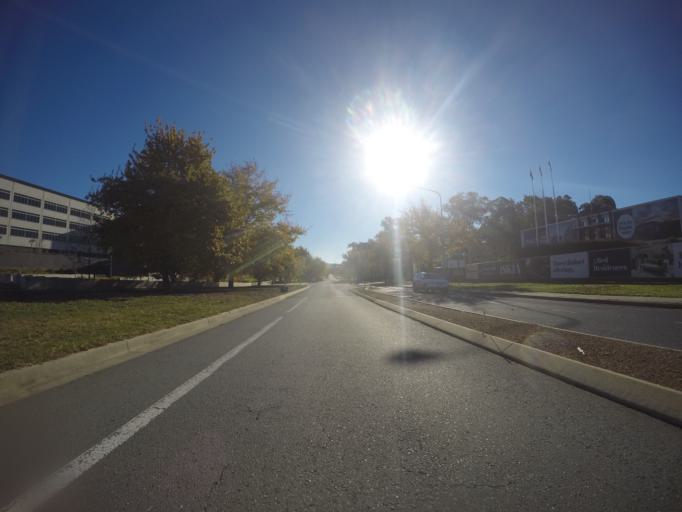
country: AU
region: Australian Capital Territory
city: Canberra
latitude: -35.2924
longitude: 149.1463
